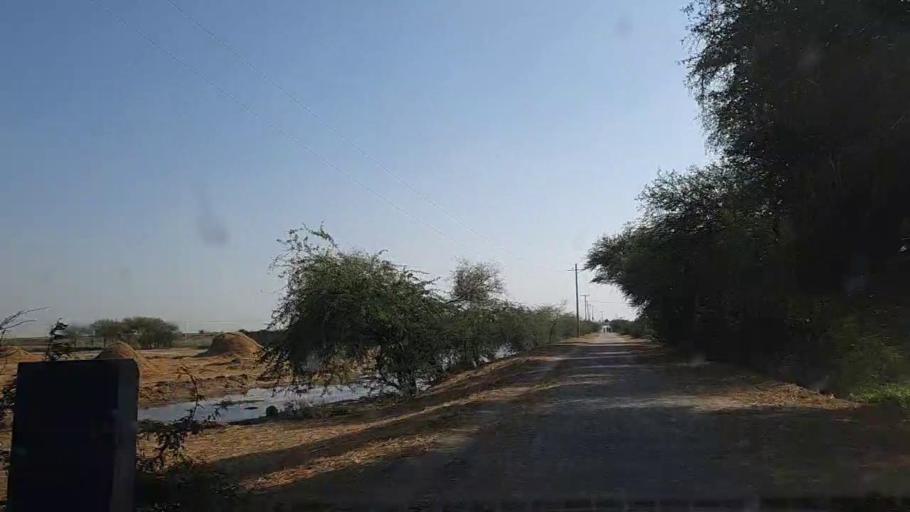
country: PK
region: Sindh
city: Thatta
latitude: 24.6212
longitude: 68.0779
